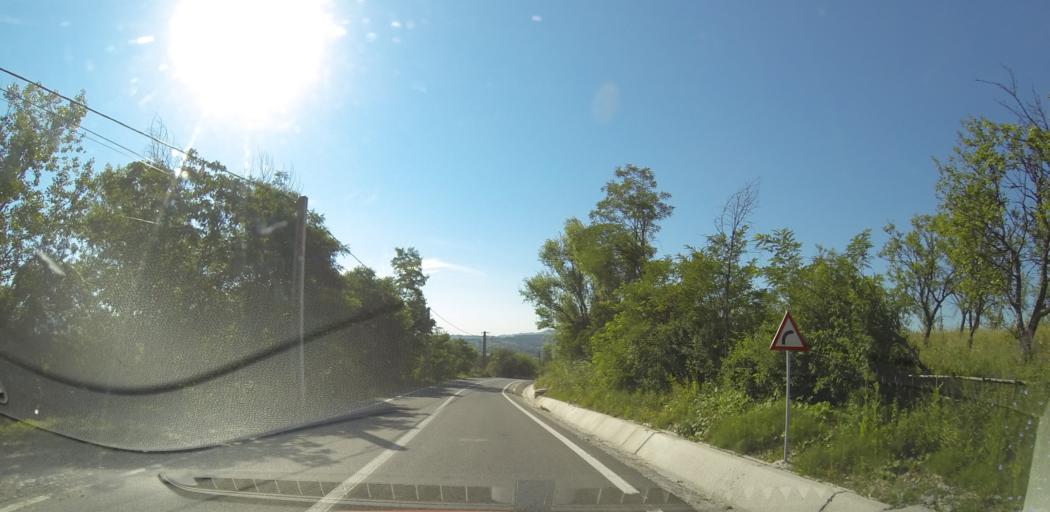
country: RO
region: Gorj
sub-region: Comuna Polovragi
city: Polovragi
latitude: 45.1748
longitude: 23.8608
